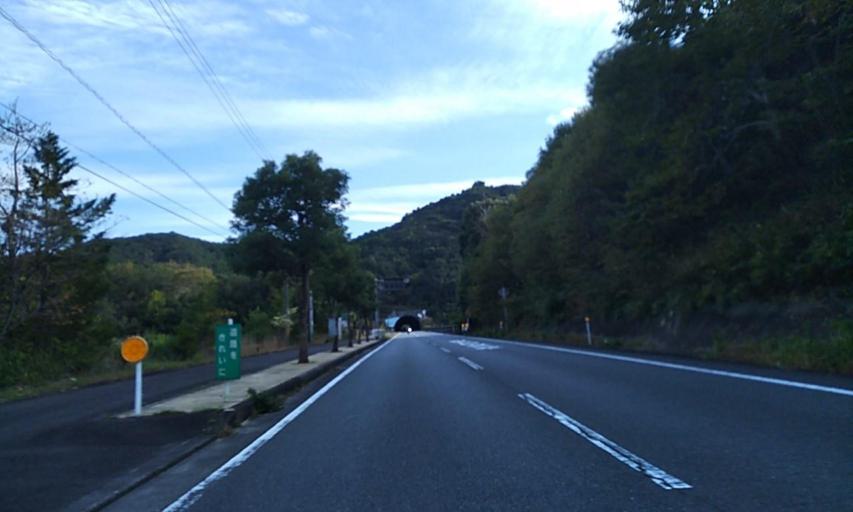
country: JP
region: Mie
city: Toba
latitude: 34.3675
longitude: 136.7938
